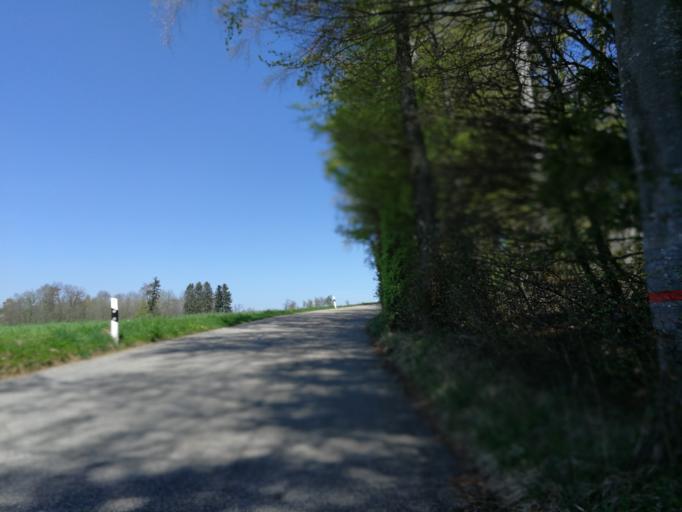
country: CH
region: Zurich
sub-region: Bezirk Uster
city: Aesch
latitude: 47.3032
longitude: 8.6419
